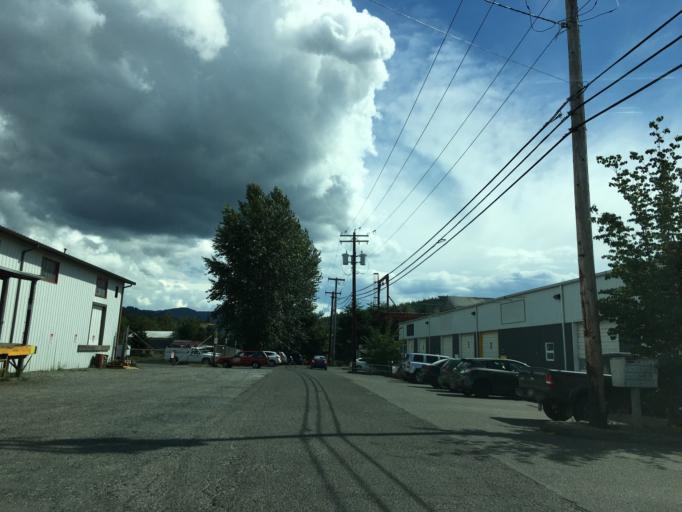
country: US
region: Washington
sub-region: Whatcom County
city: Bellingham
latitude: 48.7550
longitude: -122.4737
